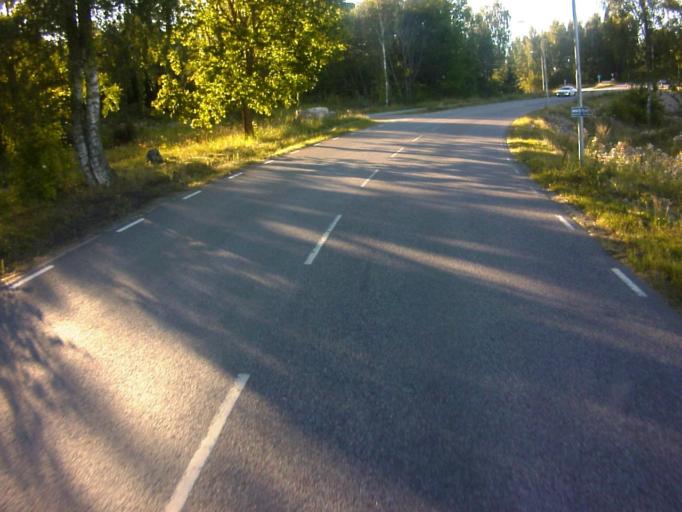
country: SE
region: Soedermanland
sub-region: Eskilstuna Kommun
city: Hallbybrunn
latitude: 59.3811
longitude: 16.4310
